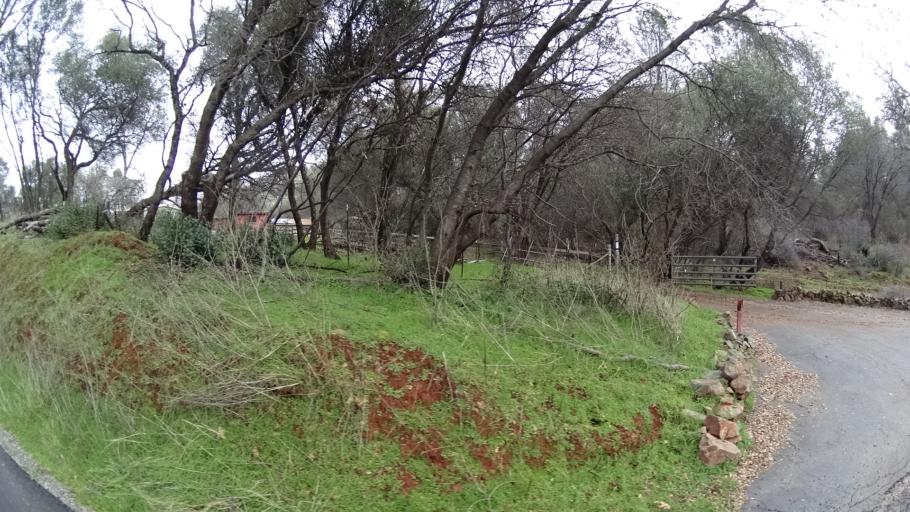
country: US
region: California
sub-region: Yuba County
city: Loma Rica
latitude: 39.3669
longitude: -121.3718
